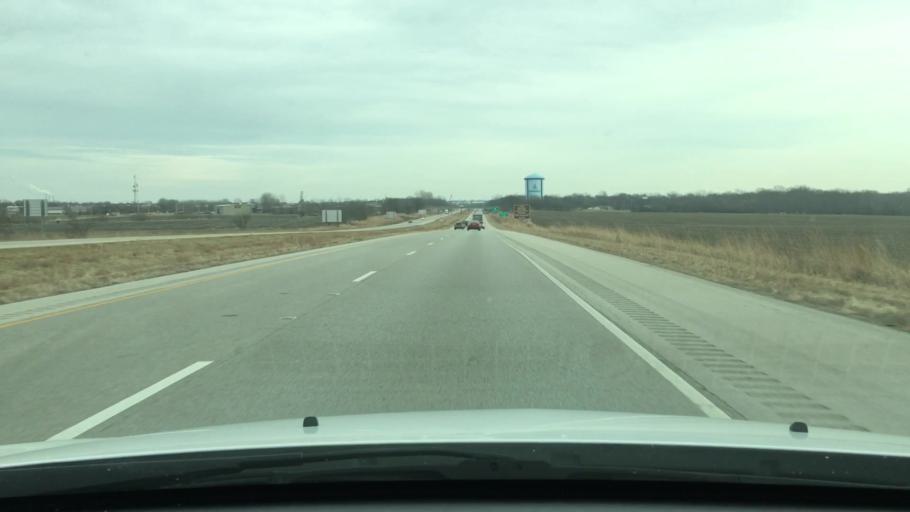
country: US
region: Illinois
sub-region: Sangamon County
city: Jerome
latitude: 39.7503
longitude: -89.7288
